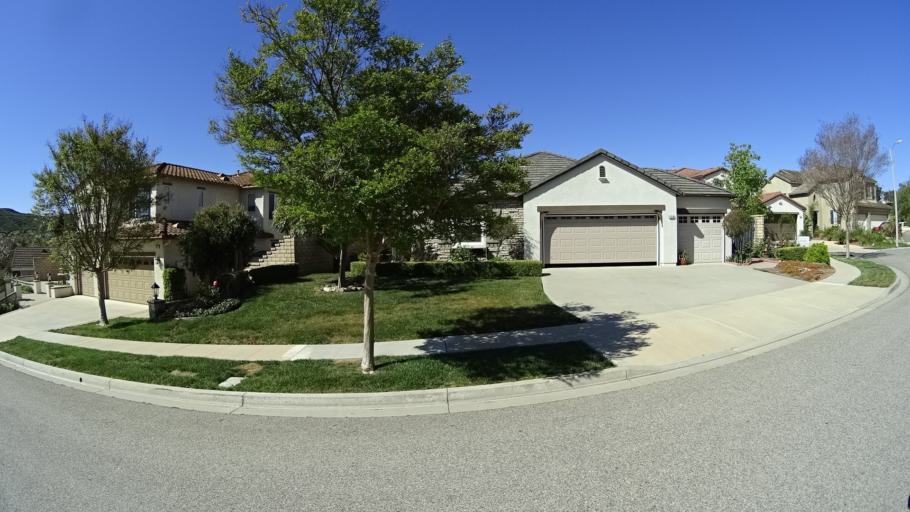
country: US
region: California
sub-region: Ventura County
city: Casa Conejo
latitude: 34.1767
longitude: -118.9794
